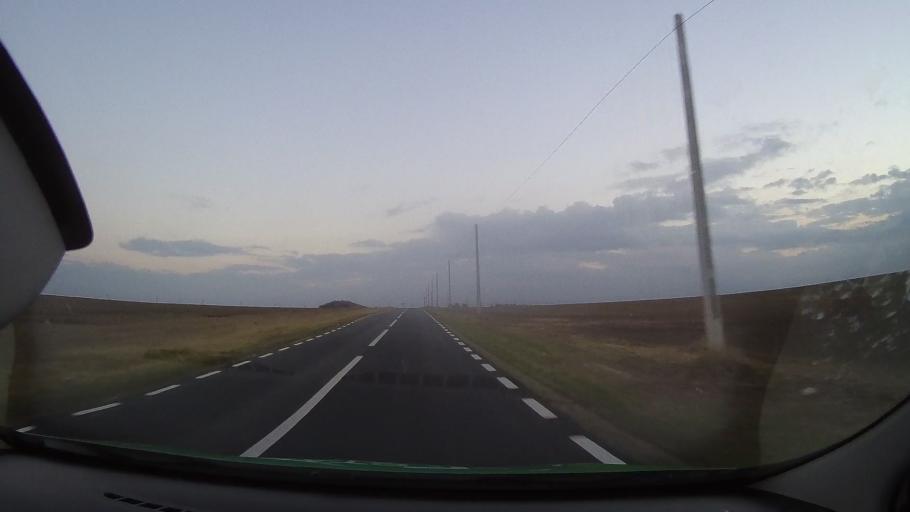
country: RO
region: Constanta
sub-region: Comuna Oltina
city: Oltina
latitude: 44.1343
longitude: 27.6674
